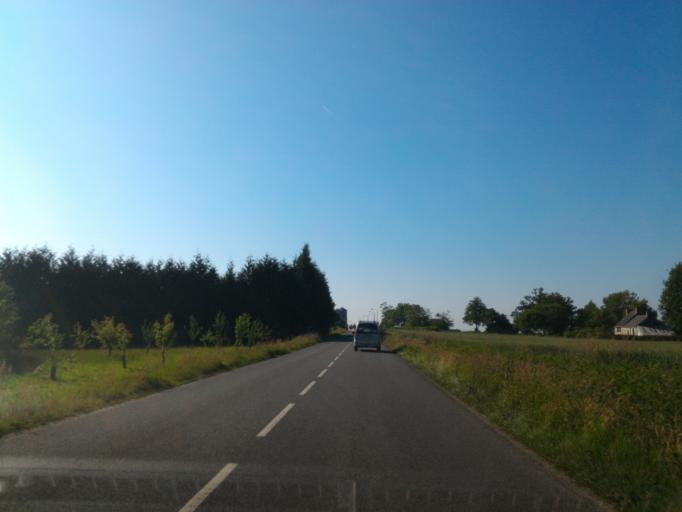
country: FR
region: Pays de la Loire
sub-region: Departement de la Mayenne
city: Juvigne
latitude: 48.2203
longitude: -1.0923
